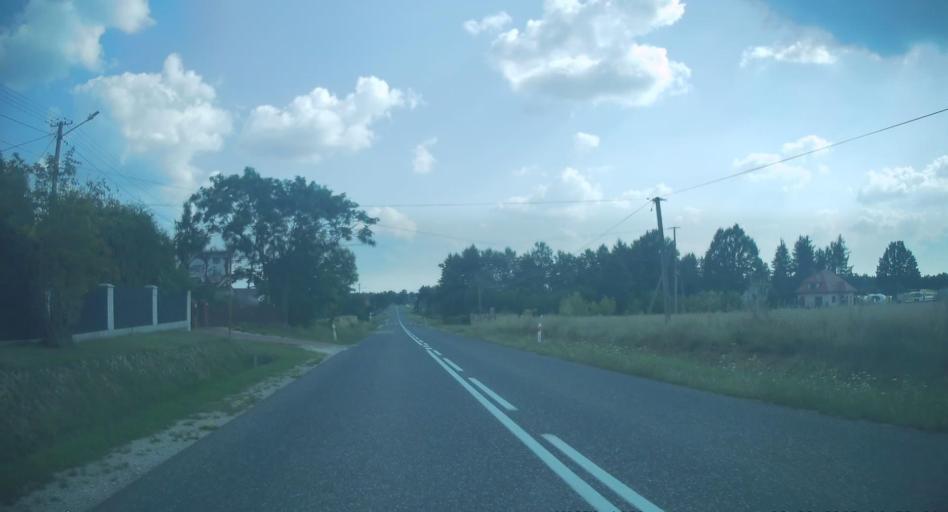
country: PL
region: Swietokrzyskie
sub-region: Powiat kielecki
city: Lopuszno
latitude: 50.9163
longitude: 20.2431
